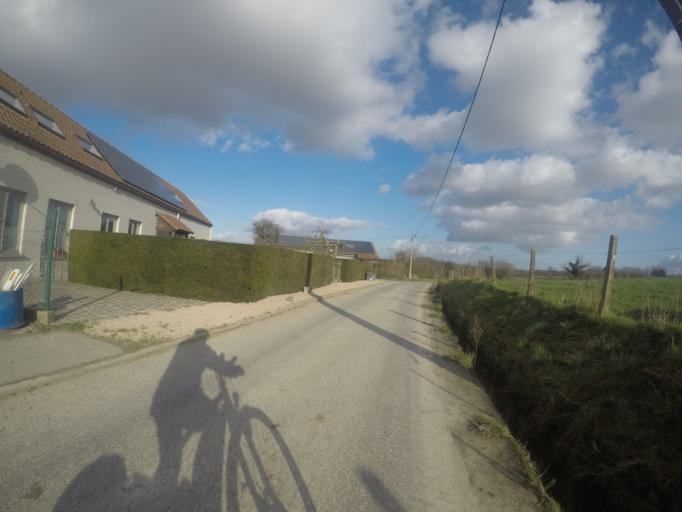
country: BE
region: Wallonia
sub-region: Province du Brabant Wallon
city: Rebecq-Rognon
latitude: 50.6447
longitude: 4.0846
